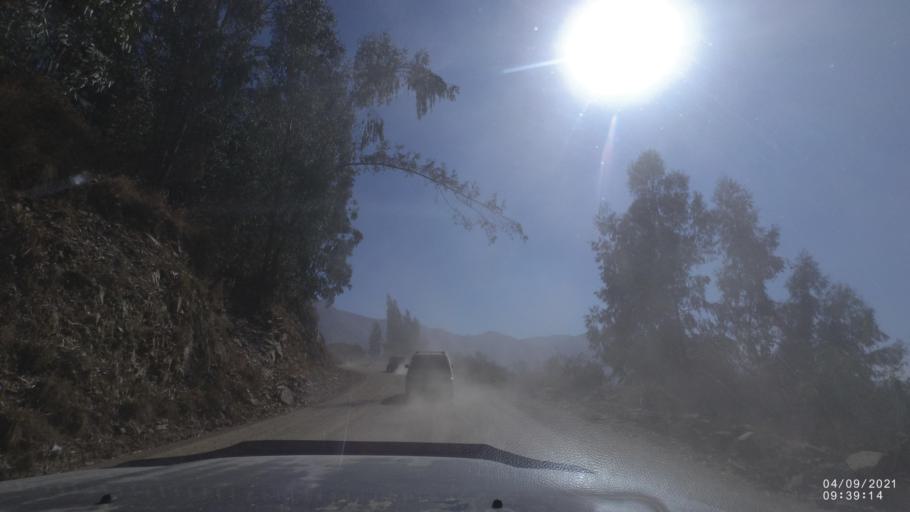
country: BO
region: Cochabamba
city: Sipe Sipe
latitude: -17.3470
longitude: -66.3851
